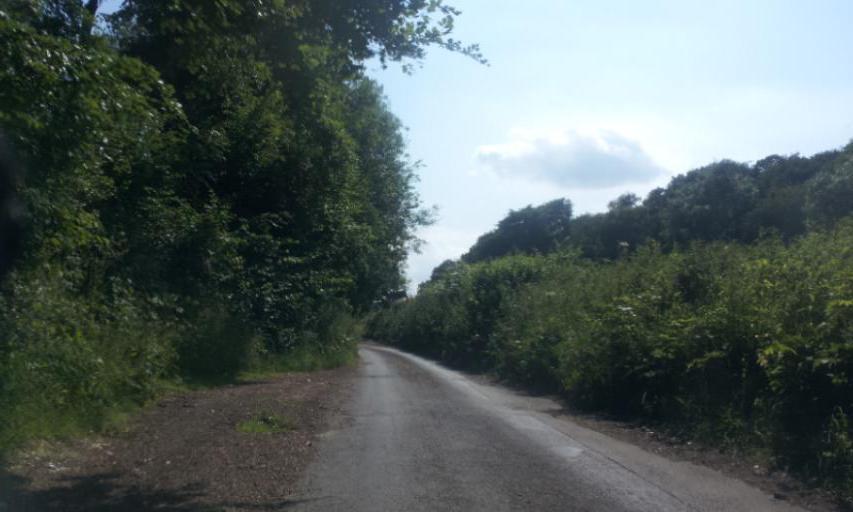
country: GB
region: England
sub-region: Kent
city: Lenham
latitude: 51.2782
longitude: 0.7664
